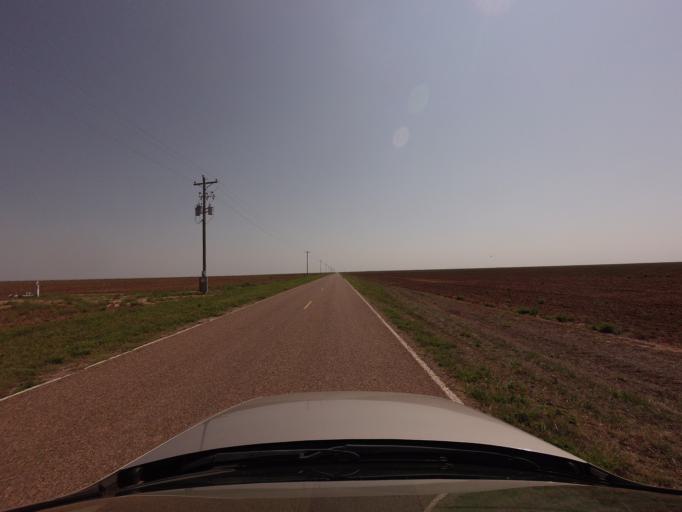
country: US
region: New Mexico
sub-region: Curry County
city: Cannon Air Force Base
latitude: 34.6327
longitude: -103.3141
